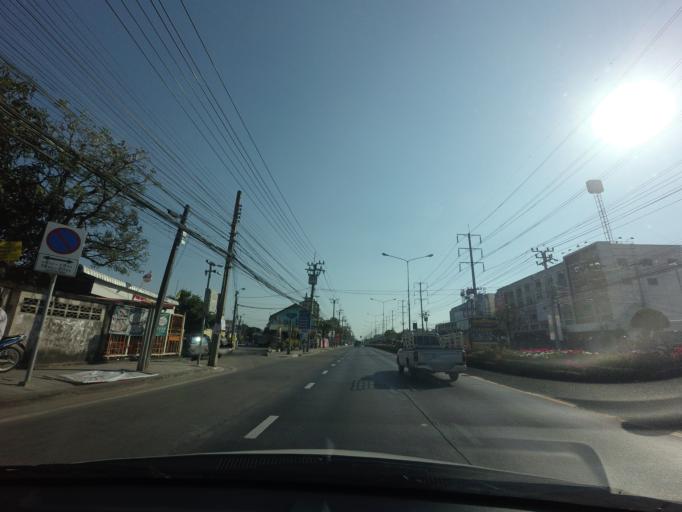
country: TH
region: Bangkok
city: Nong Chok
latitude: 13.8505
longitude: 100.8603
